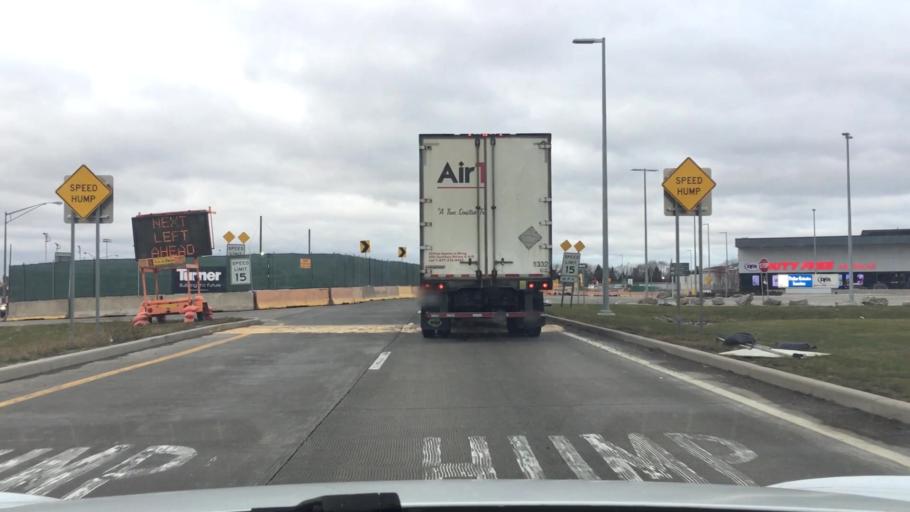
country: US
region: New York
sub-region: Niagara County
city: Lewiston
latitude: 43.1518
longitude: -79.0323
